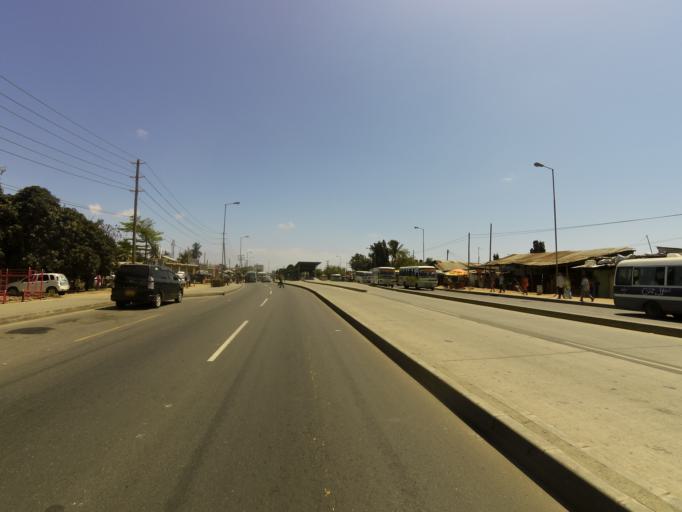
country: TZ
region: Dar es Salaam
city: Magomeni
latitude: -6.7968
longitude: 39.2637
